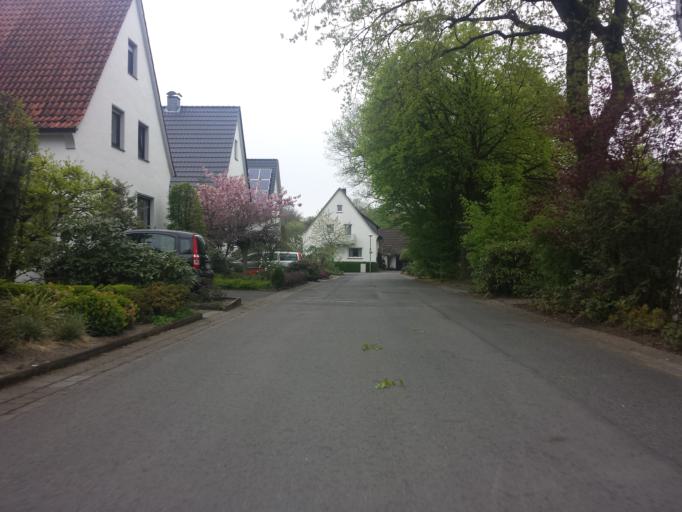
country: DE
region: North Rhine-Westphalia
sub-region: Regierungsbezirk Detmold
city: Guetersloh
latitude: 51.8932
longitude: 8.3893
